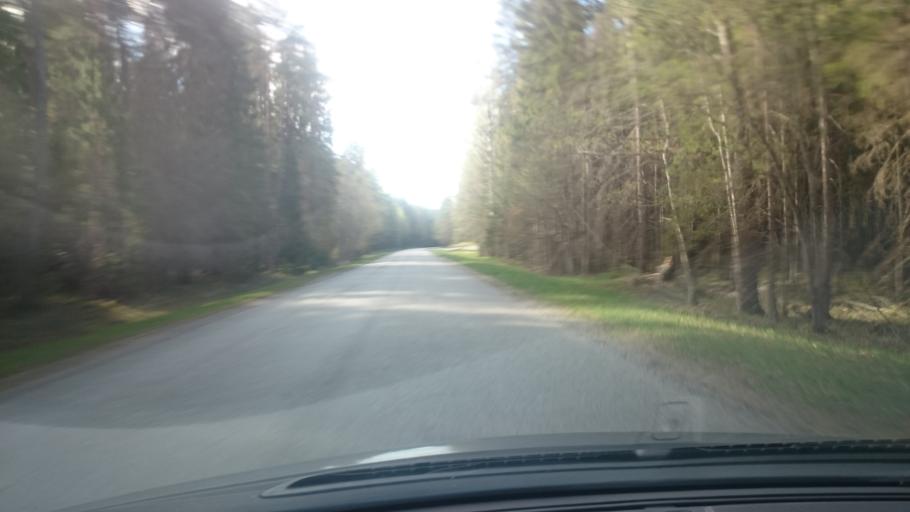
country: EE
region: Ida-Virumaa
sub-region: Toila vald
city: Voka
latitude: 59.1603
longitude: 27.5954
